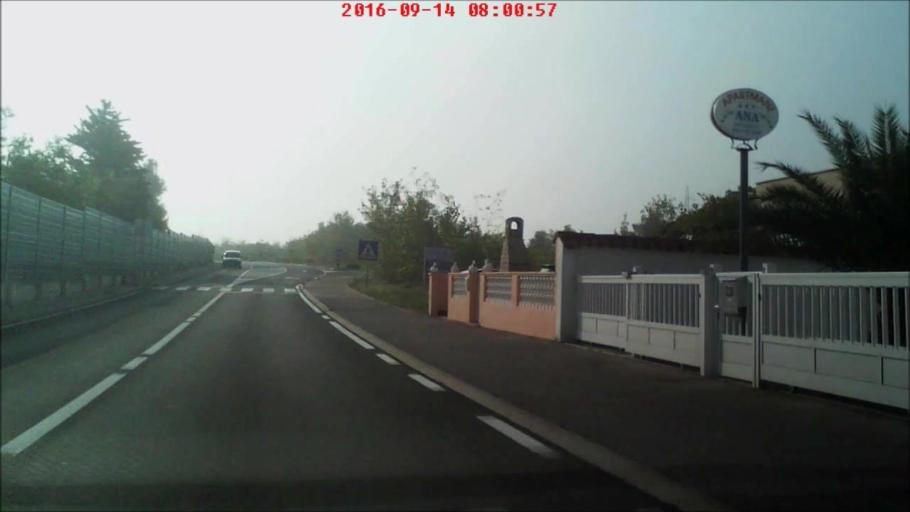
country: HR
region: Zadarska
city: Nin
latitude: 44.2549
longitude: 15.1566
